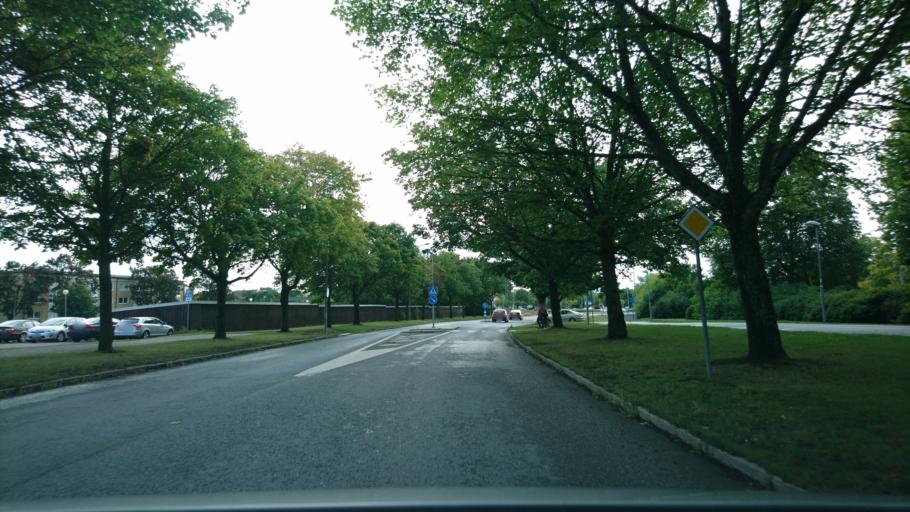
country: SE
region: Uppsala
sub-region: Uppsala Kommun
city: Uppsala
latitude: 59.8770
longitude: 17.6452
